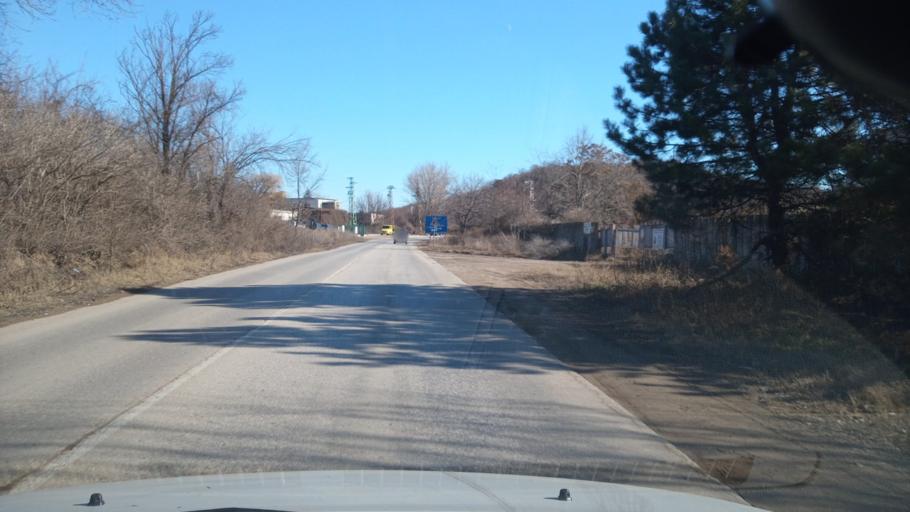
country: BG
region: Pleven
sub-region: Obshtina Pleven
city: Pleven
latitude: 43.4398
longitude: 24.5949
